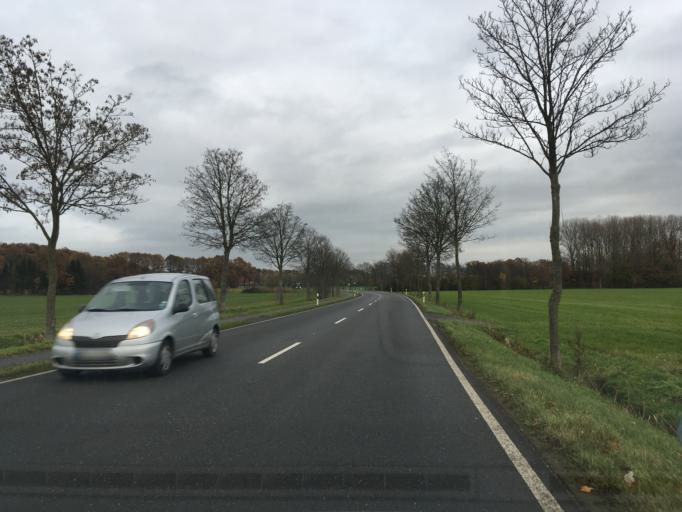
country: DE
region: North Rhine-Westphalia
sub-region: Regierungsbezirk Munster
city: Gescher
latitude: 51.9754
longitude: 7.0202
